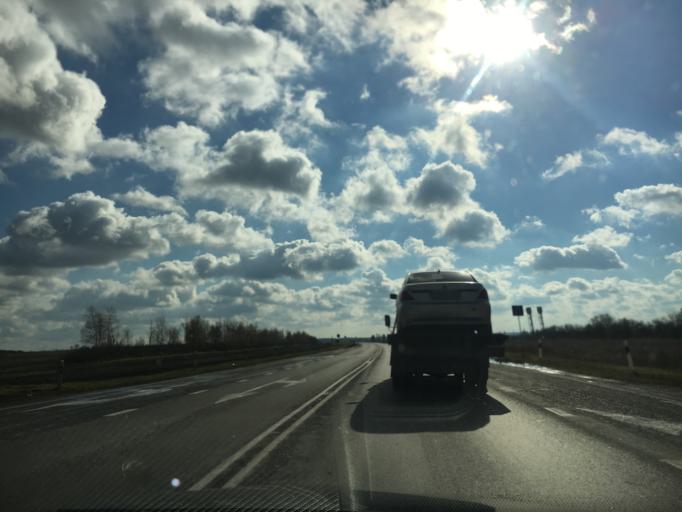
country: RU
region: Rostov
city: Matveyev Kurgan
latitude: 47.5194
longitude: 38.8981
